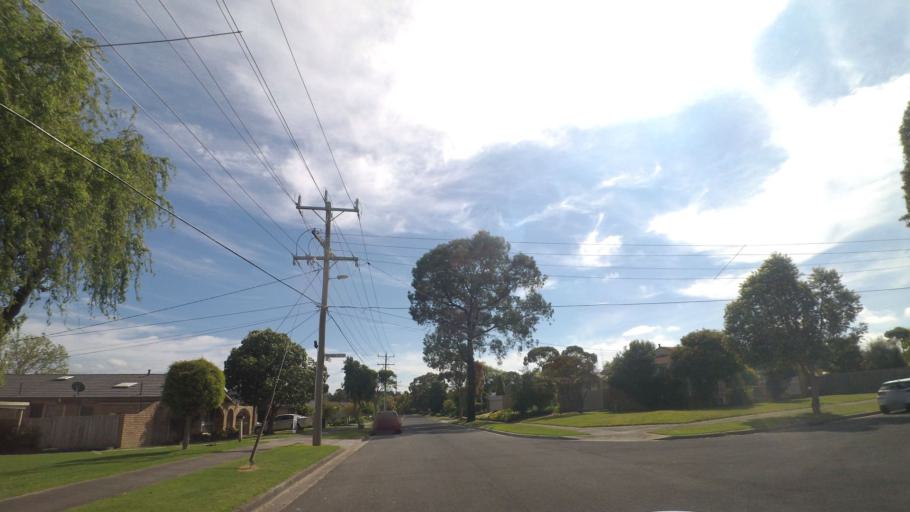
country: AU
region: Victoria
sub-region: Knox
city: Bayswater
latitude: -37.8541
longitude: 145.2573
